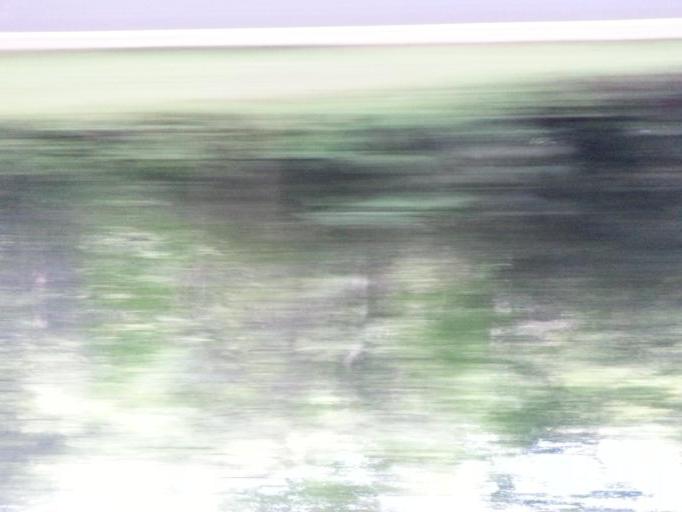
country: US
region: Tennessee
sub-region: Johnson County
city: Mountain City
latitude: 36.5669
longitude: -81.8714
